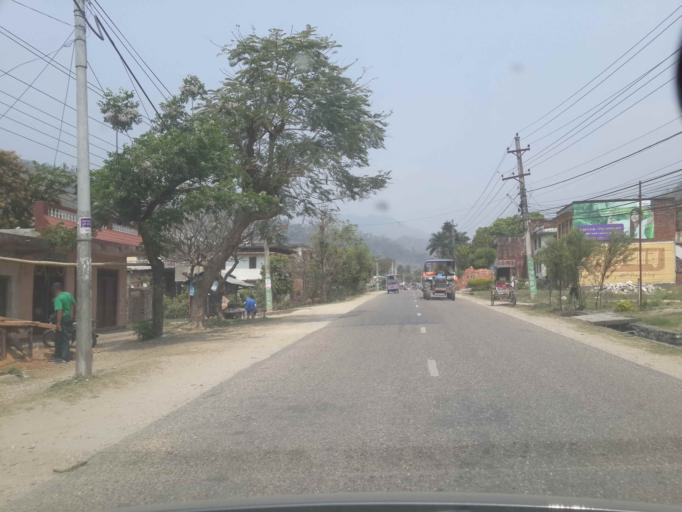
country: NP
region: Central Region
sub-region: Narayani Zone
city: Hitura
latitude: 27.4384
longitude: 85.0350
